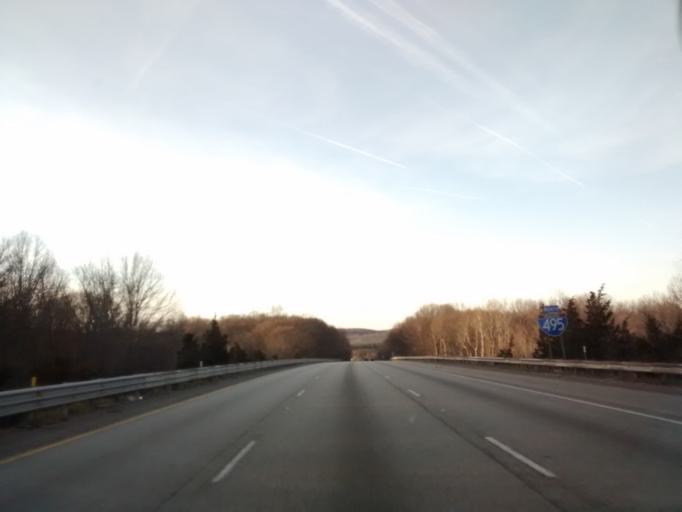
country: US
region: Massachusetts
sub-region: Worcester County
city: Southborough
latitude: 42.2948
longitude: -71.5660
